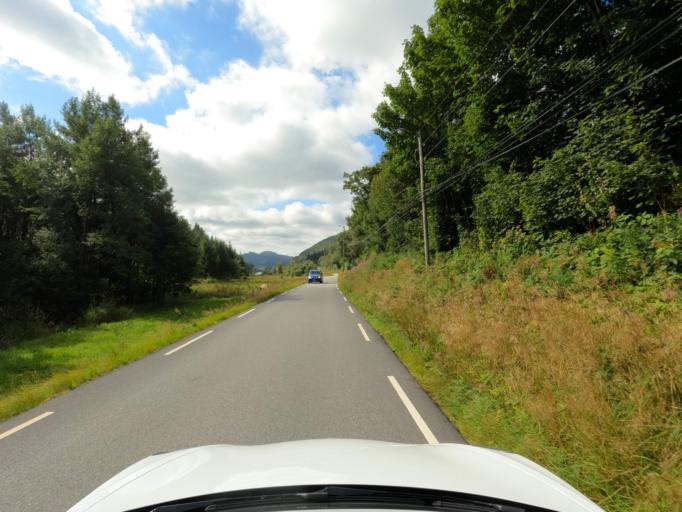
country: NO
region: Hordaland
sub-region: Os
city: Syfteland
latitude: 60.2874
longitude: 5.4726
